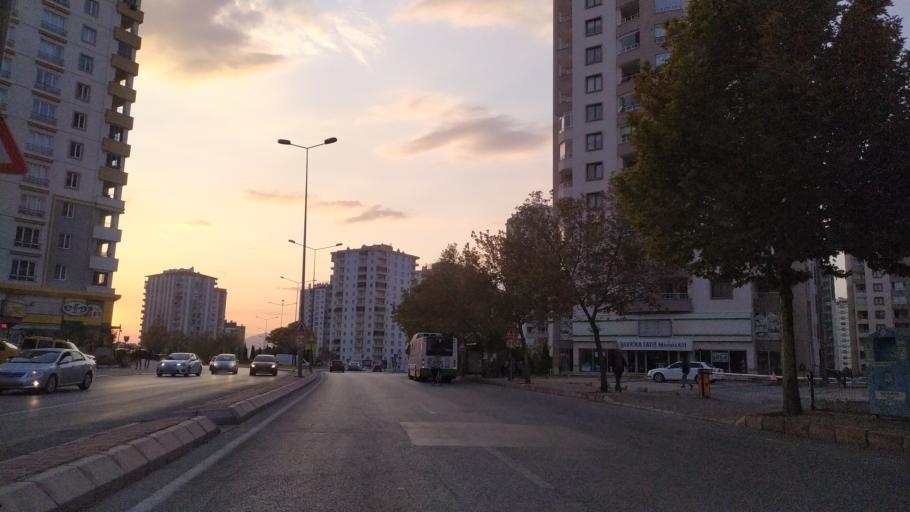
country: TR
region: Kayseri
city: Talas
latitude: 38.7086
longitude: 35.5623
